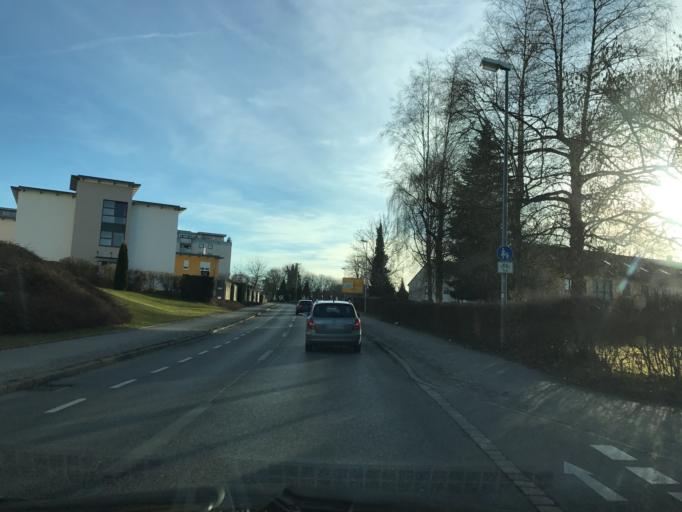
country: DE
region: Baden-Wuerttemberg
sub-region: Tuebingen Region
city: Bad Waldsee
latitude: 47.9153
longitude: 9.7472
